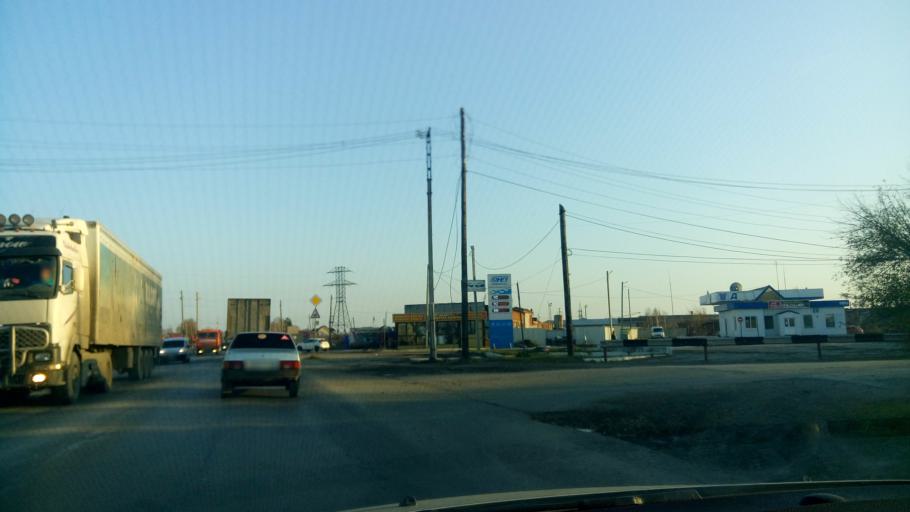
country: RU
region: Sverdlovsk
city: Bogdanovich
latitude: 56.7622
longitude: 62.0712
